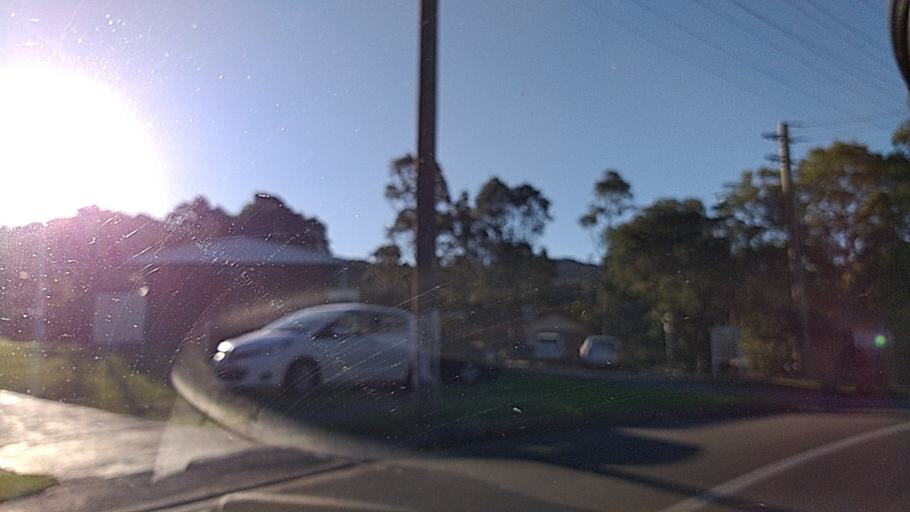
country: AU
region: New South Wales
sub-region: Wollongong
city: Mount Keira
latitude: -34.4257
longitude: 150.8462
